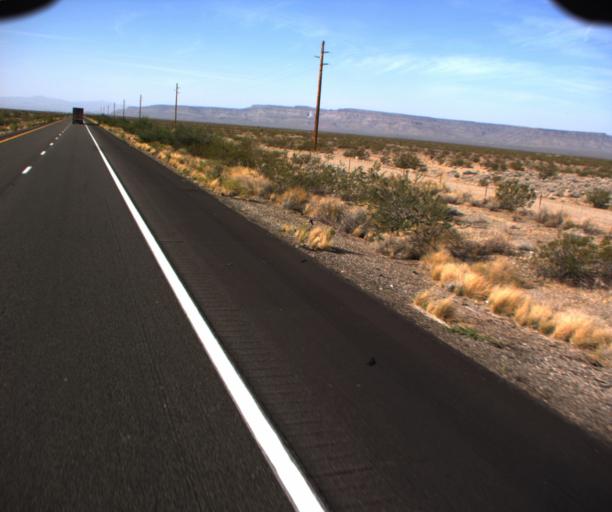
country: US
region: Arizona
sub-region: Mohave County
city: Kingman
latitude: 35.0010
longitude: -114.1369
